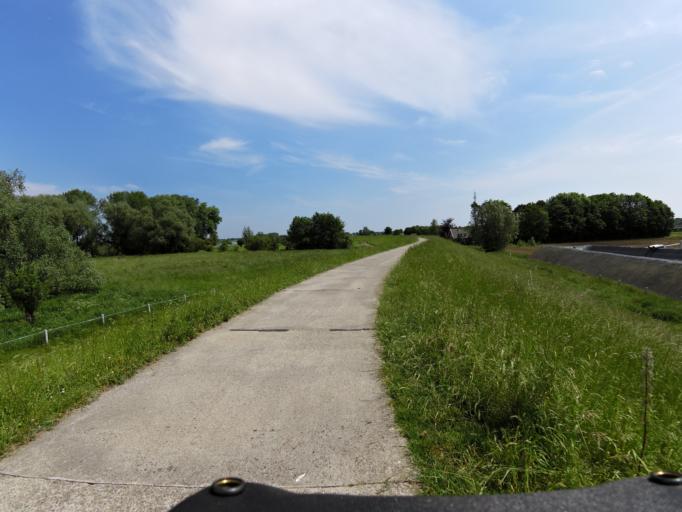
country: NL
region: South Holland
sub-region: Gemeente Leerdam
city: Leerdam
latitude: 51.8230
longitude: 5.0791
